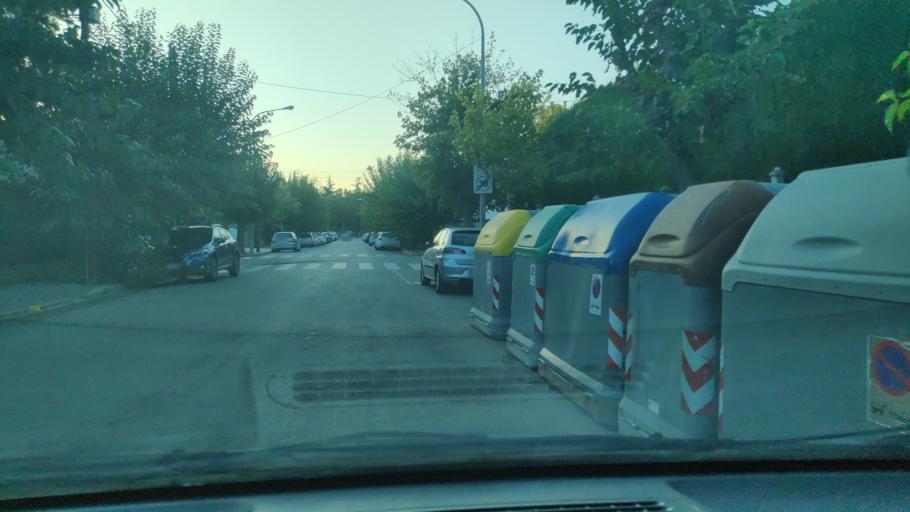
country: ES
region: Catalonia
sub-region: Provincia de Barcelona
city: Cerdanyola del Valles
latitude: 41.4854
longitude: 2.1396
